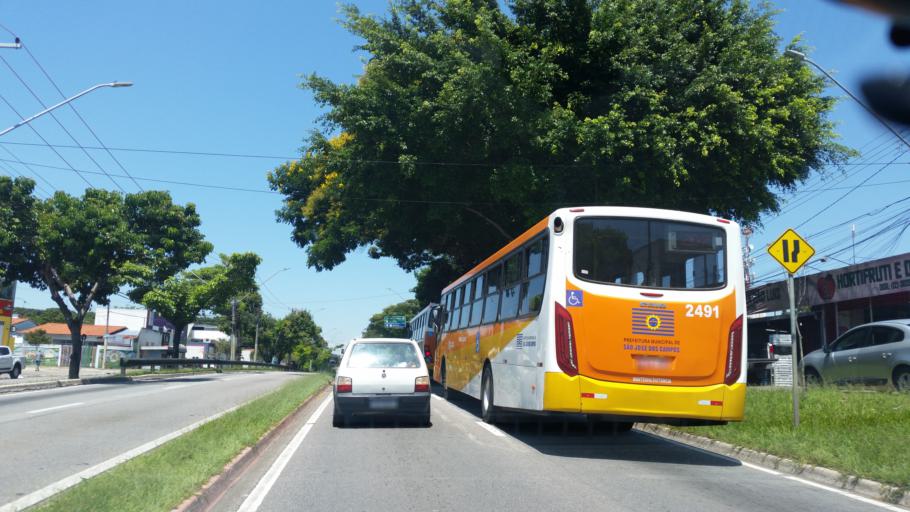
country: BR
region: Sao Paulo
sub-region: Sao Jose Dos Campos
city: Sao Jose dos Campos
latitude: -23.1757
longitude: -45.8243
